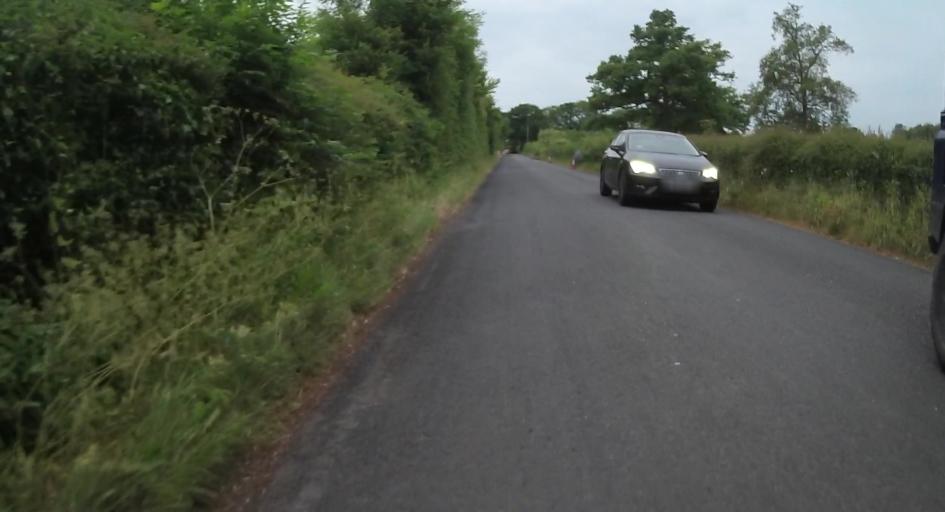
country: GB
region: England
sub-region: Hampshire
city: Odiham
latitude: 51.2530
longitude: -0.8926
